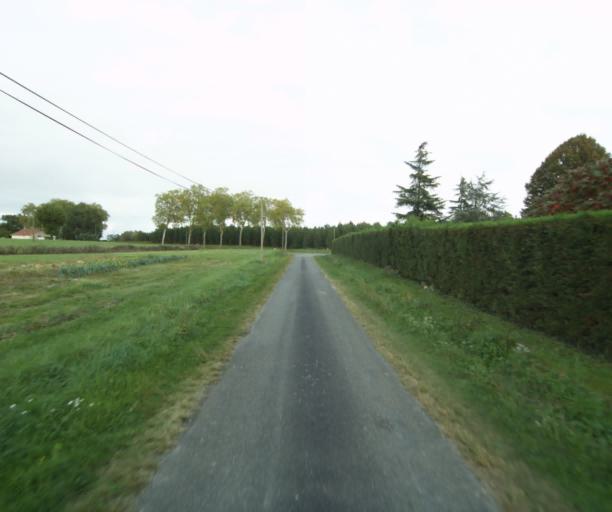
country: FR
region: Aquitaine
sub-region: Departement des Landes
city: Gabarret
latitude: 43.9688
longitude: 0.0899
